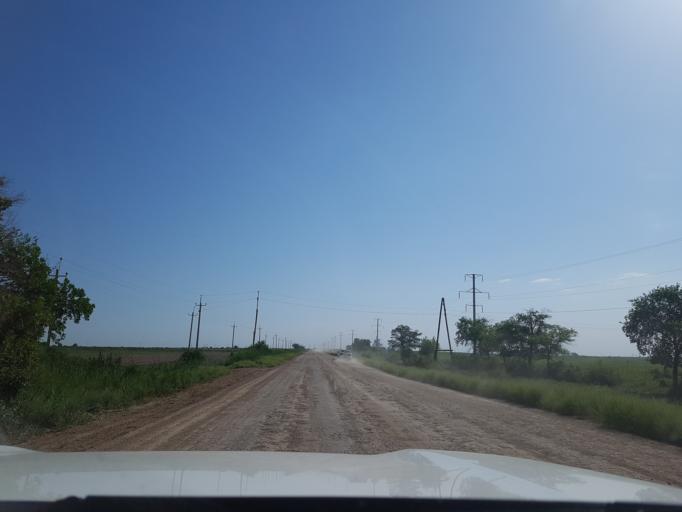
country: TM
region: Dasoguz
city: Koeneuergench
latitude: 42.1299
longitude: 58.9450
